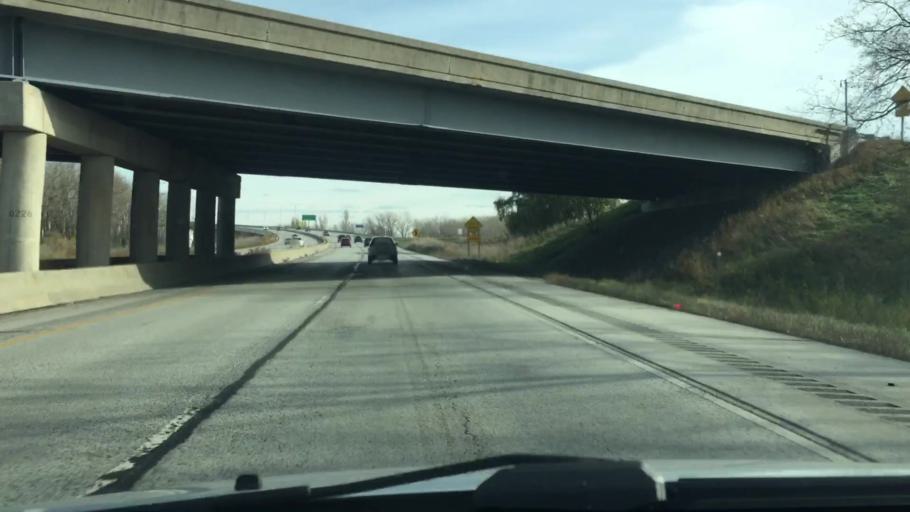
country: US
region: Wisconsin
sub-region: Brown County
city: Green Bay
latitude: 44.5397
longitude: -88.0251
